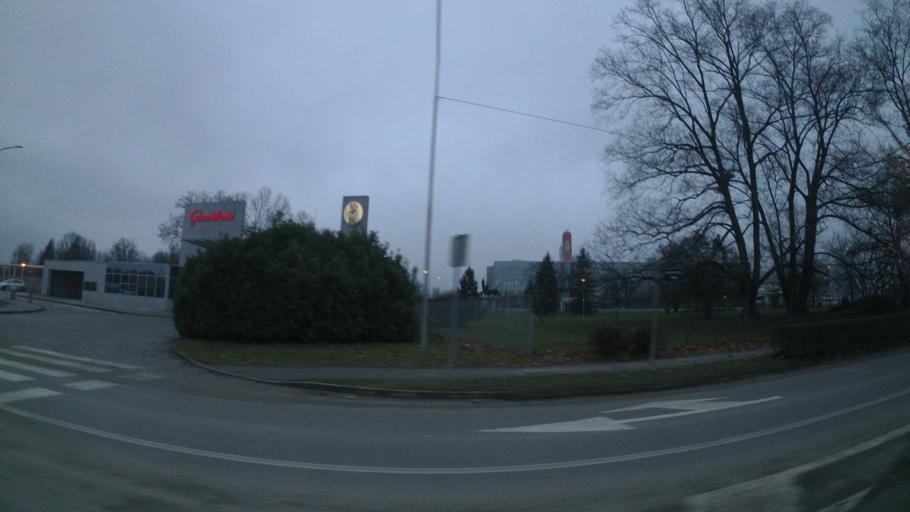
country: HR
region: Sisacko-Moslavacka
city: Petrinja
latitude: 45.4416
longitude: 16.2919
